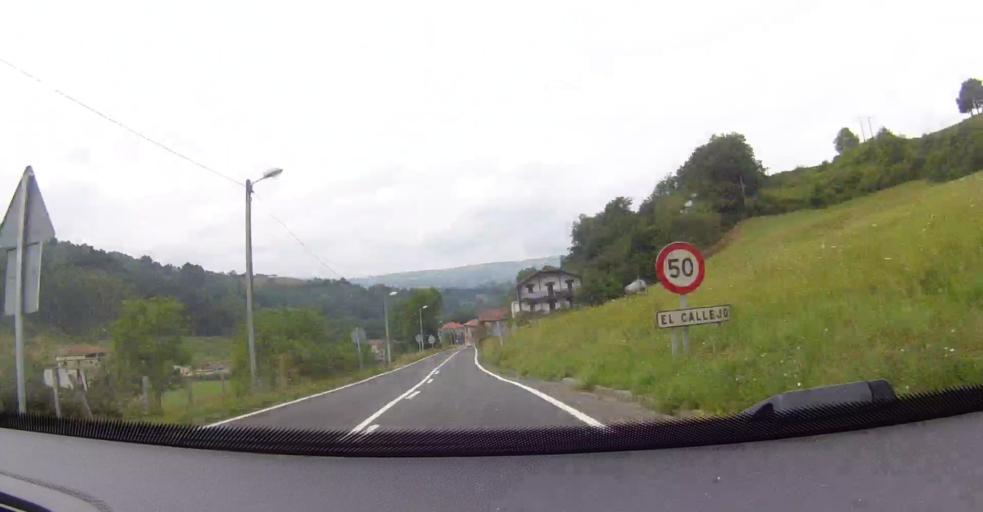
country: ES
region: Basque Country
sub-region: Bizkaia
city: Lanestosa
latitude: 43.2342
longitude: -3.3383
